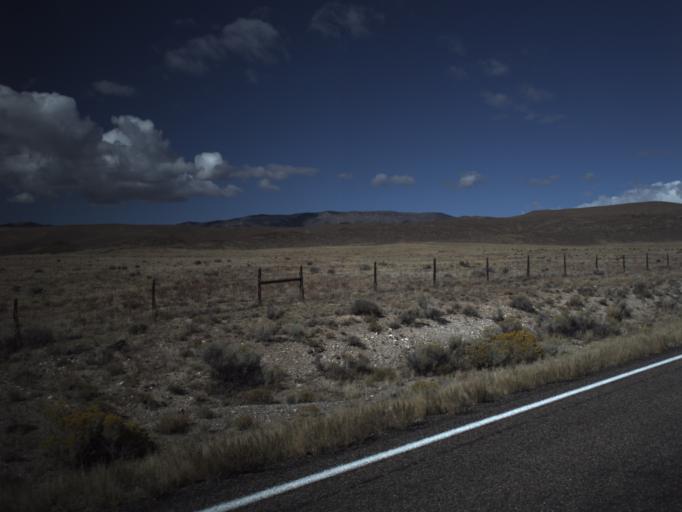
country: US
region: Utah
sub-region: Beaver County
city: Milford
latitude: 38.5912
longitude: -113.8202
